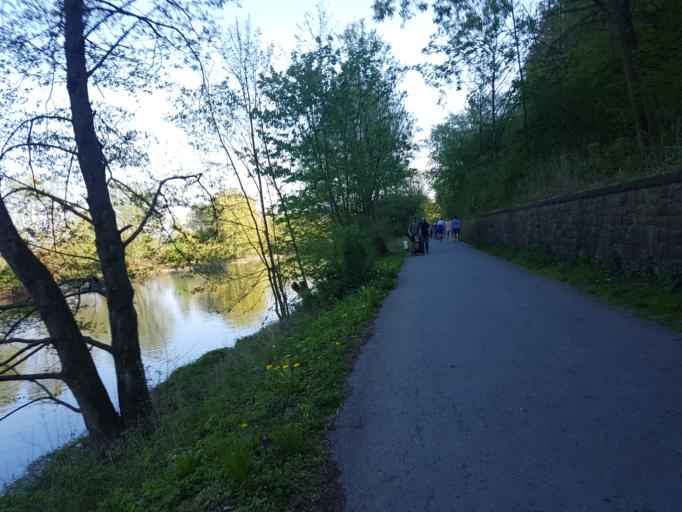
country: DE
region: North Rhine-Westphalia
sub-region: Regierungsbezirk Dusseldorf
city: Essen
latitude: 51.4332
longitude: 7.0862
